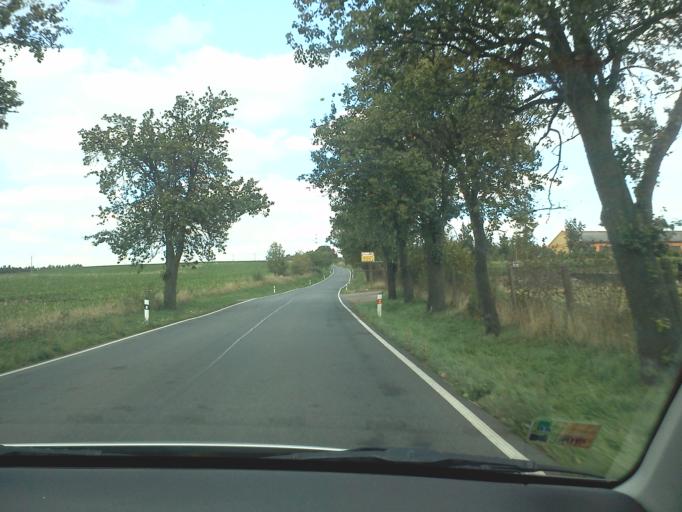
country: CZ
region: Central Bohemia
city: Cesky Brod
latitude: 50.0823
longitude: 14.8647
